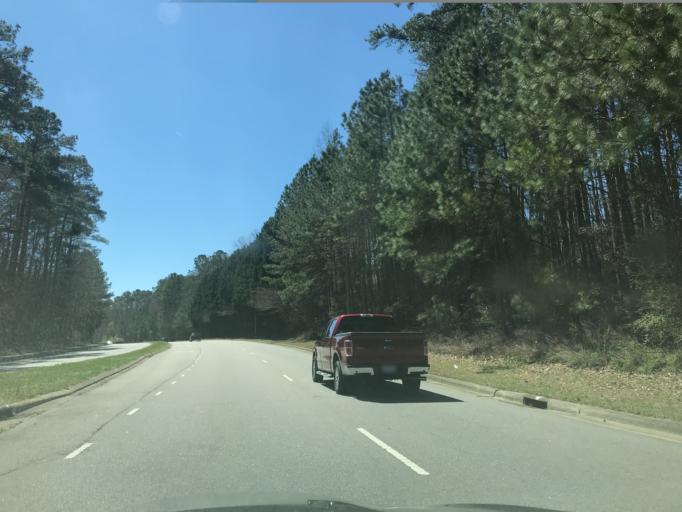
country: US
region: North Carolina
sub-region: Wake County
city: Garner
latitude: 35.6988
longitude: -78.6400
